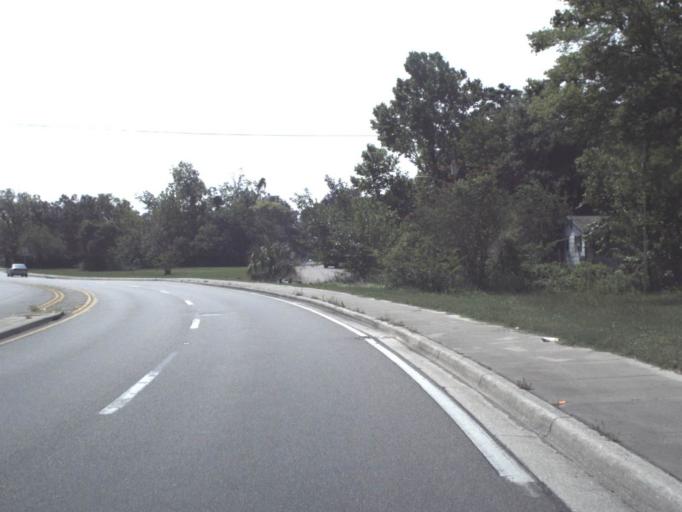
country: US
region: Florida
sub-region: Duval County
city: Jacksonville
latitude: 30.3531
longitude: -81.7073
